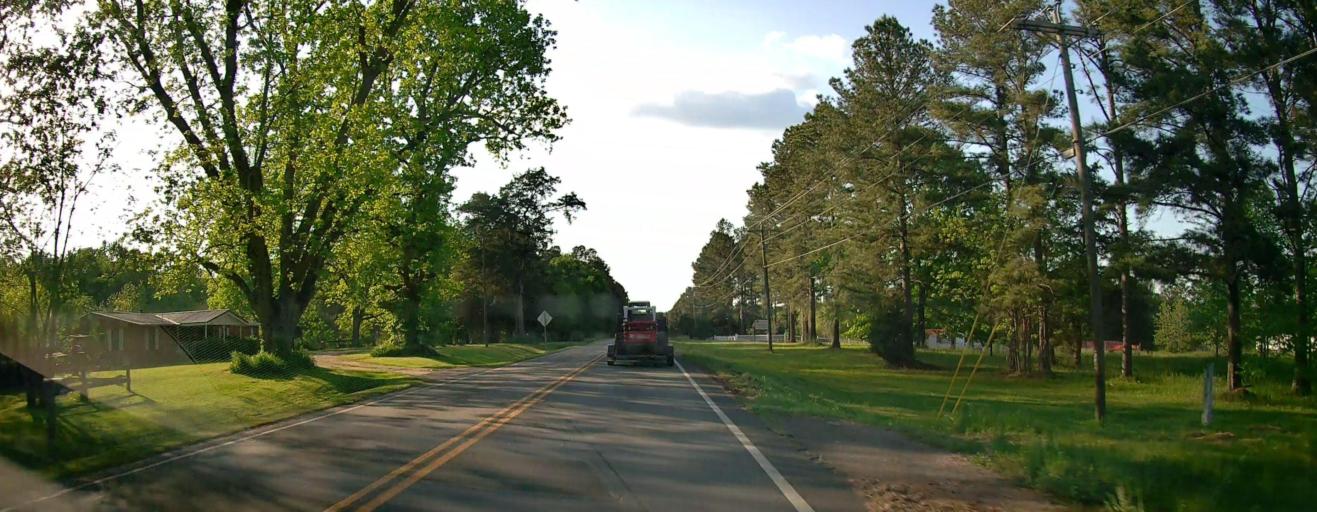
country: US
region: Georgia
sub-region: Putnam County
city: Eatonton
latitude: 33.3134
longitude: -83.4920
